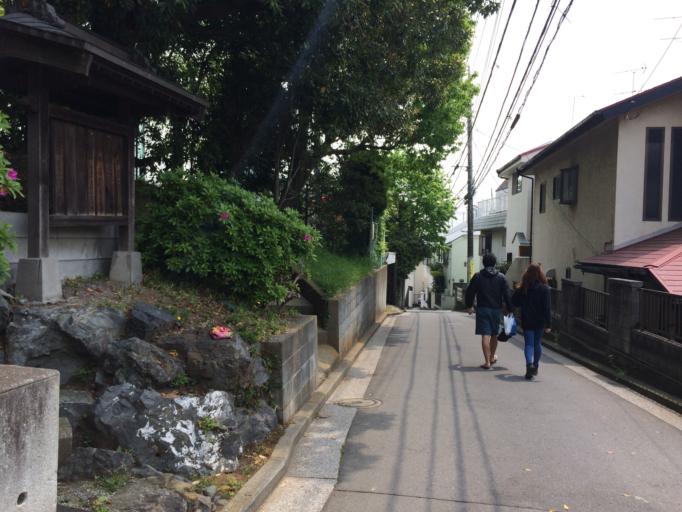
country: JP
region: Kanagawa
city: Yokohama
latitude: 35.5115
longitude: 139.6383
